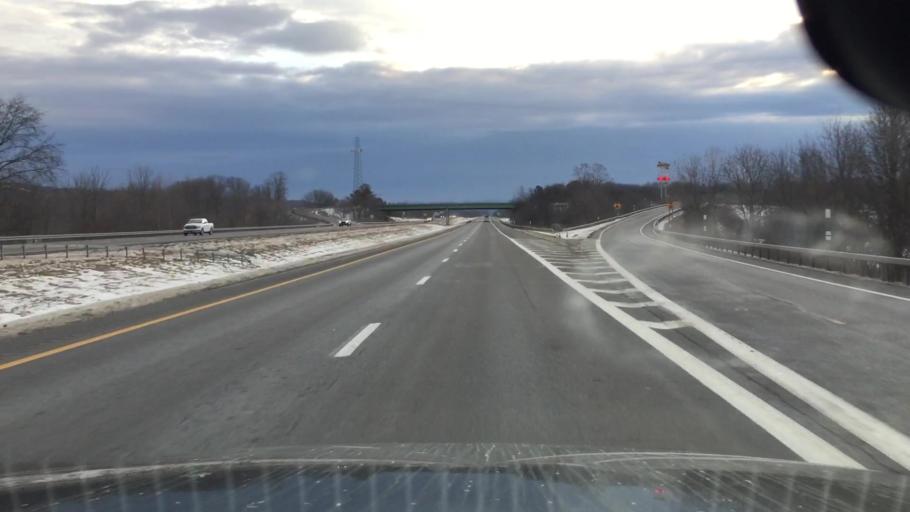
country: US
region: Pennsylvania
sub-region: Bradford County
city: South Waverly
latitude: 42.0008
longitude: -76.5919
